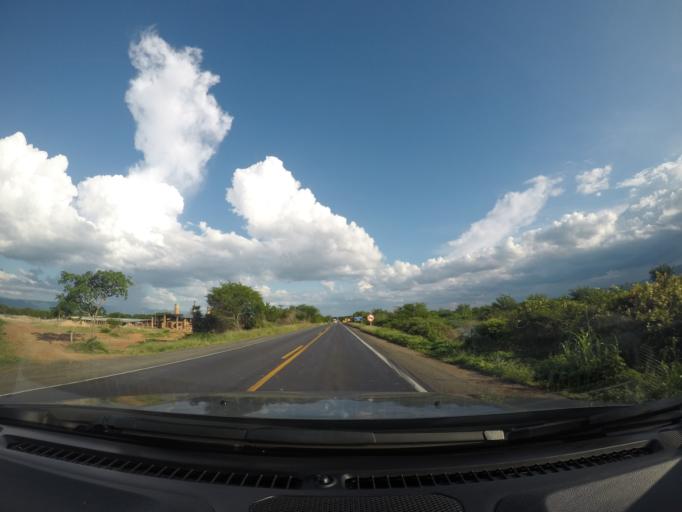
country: BR
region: Bahia
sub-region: Oliveira Dos Brejinhos
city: Oliveira dos Brejinhos
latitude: -12.0967
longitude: -42.9235
